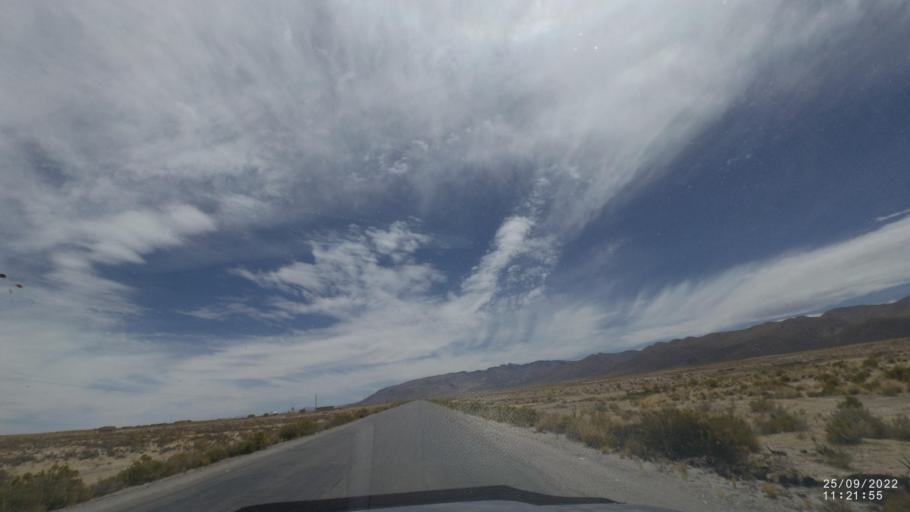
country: BO
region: Oruro
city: Challapata
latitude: -19.1351
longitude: -66.7693
